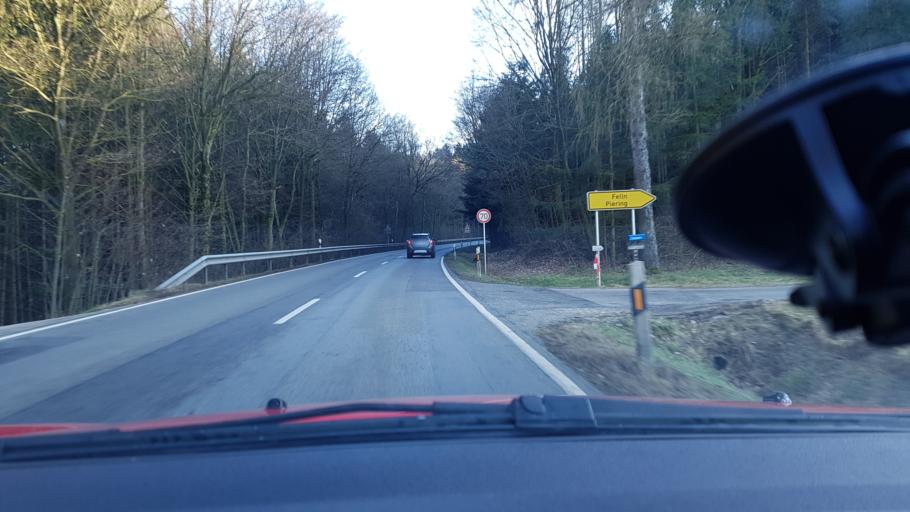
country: DE
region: Bavaria
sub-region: Lower Bavaria
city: Reut
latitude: 48.3025
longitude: 12.9649
